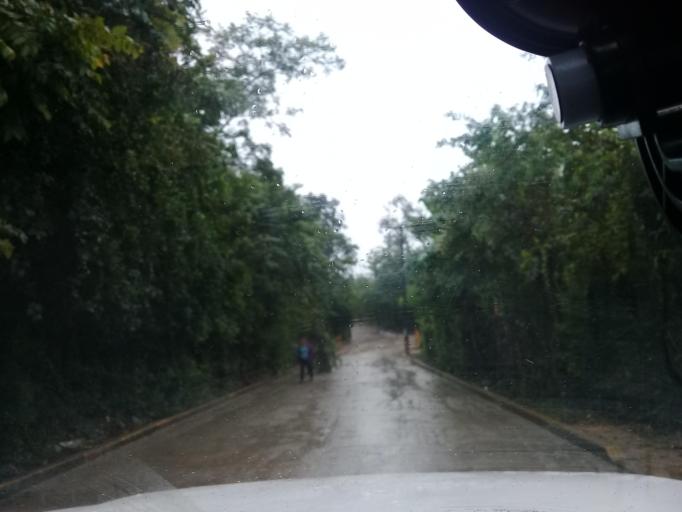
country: MX
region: Veracruz
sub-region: Chalma
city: San Pedro Coyutla
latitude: 21.1829
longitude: -98.4347
